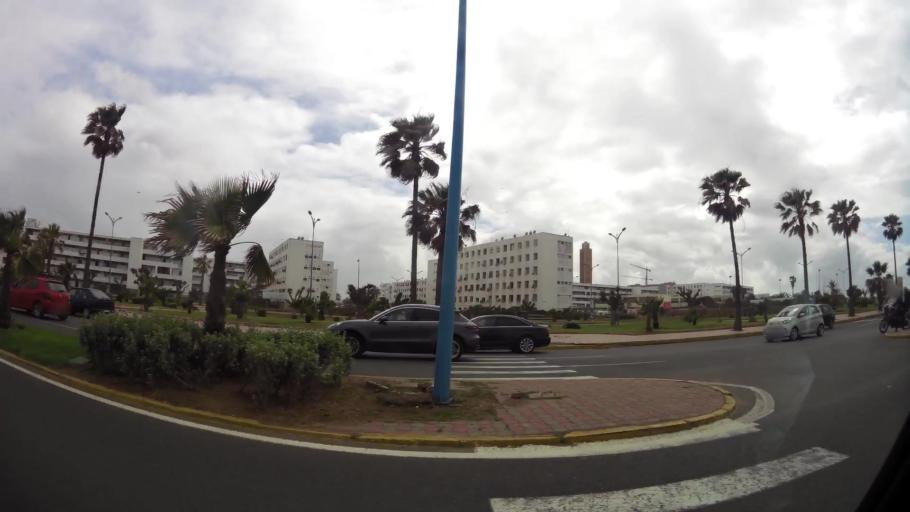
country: MA
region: Grand Casablanca
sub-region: Casablanca
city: Casablanca
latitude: 33.6066
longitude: -7.6500
